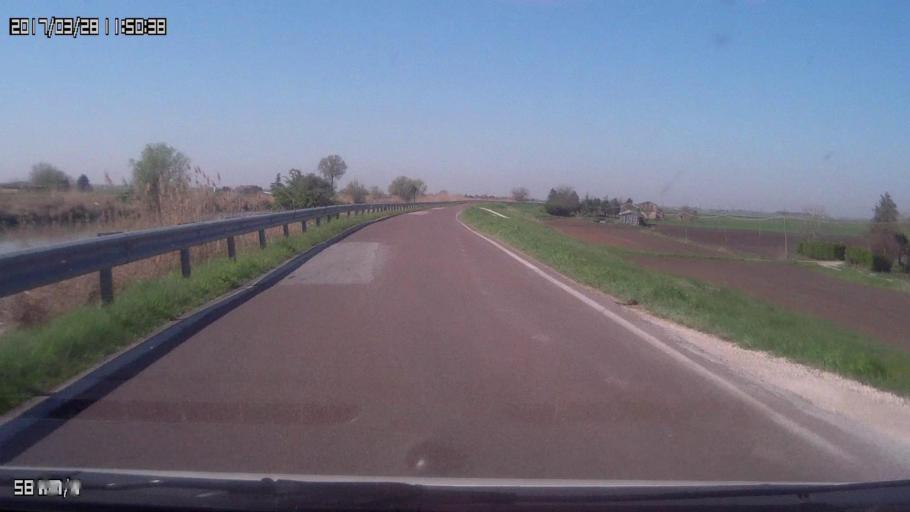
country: IT
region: Veneto
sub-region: Provincia di Venezia
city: Valli
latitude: 45.1520
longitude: 12.2005
